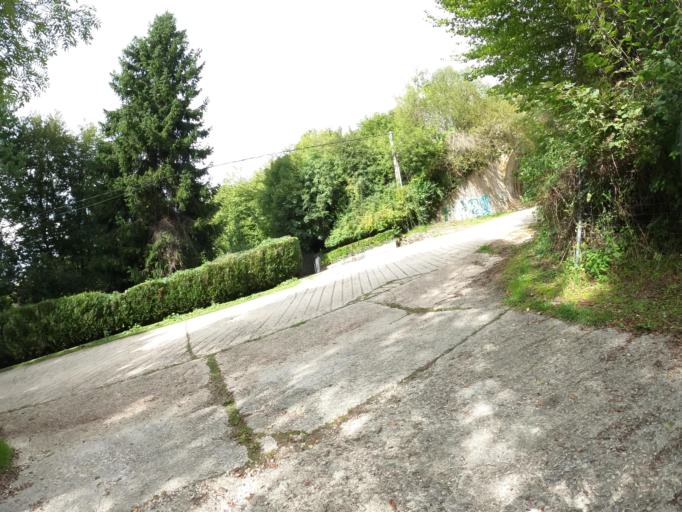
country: ES
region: Navarre
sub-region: Provincia de Navarra
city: Lekunberri
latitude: 43.0078
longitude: -1.8937
